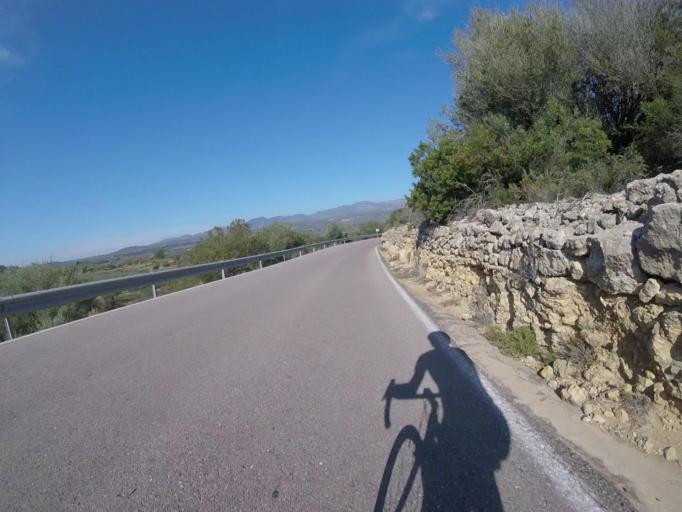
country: ES
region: Valencia
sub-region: Provincia de Castello
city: Benlloch
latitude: 40.2461
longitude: 0.0774
